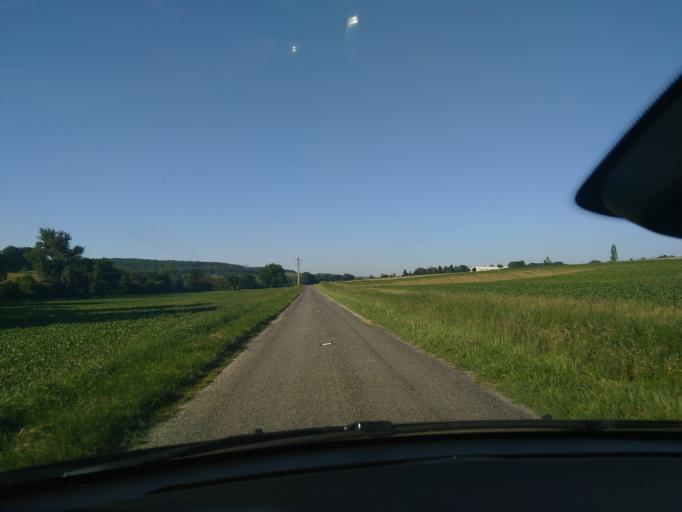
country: FR
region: Midi-Pyrenees
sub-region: Departement du Tarn-et-Garonne
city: Beaumont-de-Lomagne
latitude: 43.8385
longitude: 1.0712
